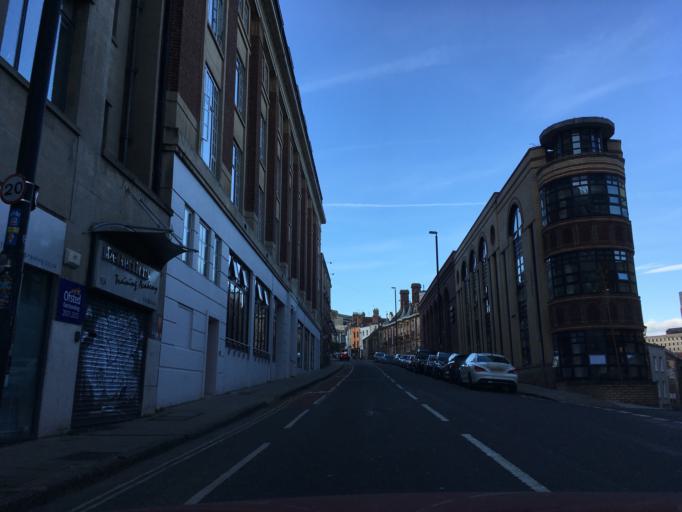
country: GB
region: England
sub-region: Bristol
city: Bristol
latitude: 51.4549
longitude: -2.5977
